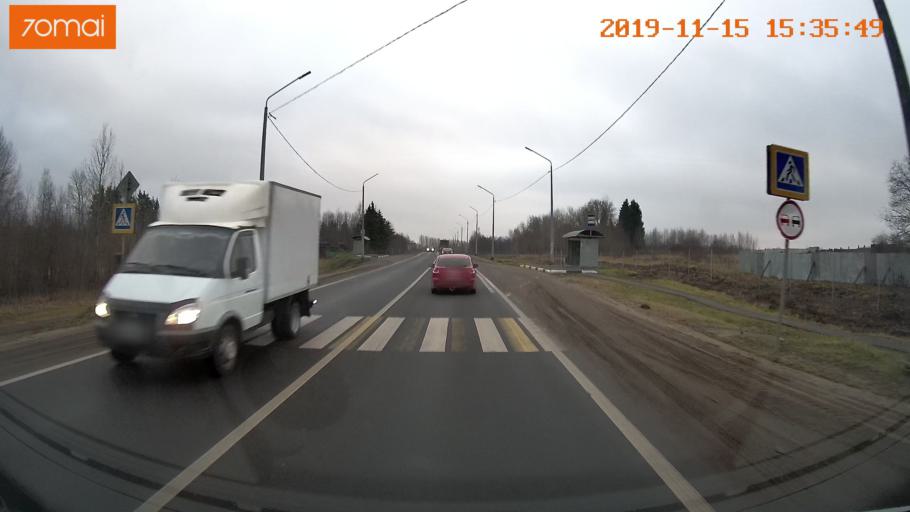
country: RU
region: Jaroslavl
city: Danilov
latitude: 58.0553
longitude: 40.0882
